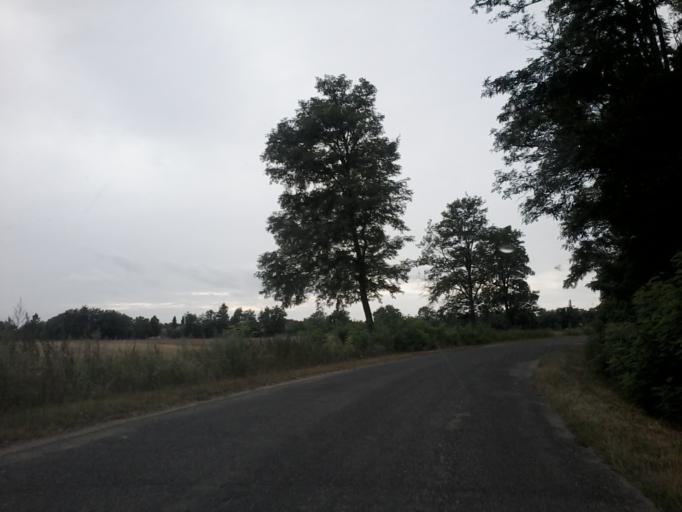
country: HU
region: Vas
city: Celldomolk
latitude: 47.2082
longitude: 17.0762
